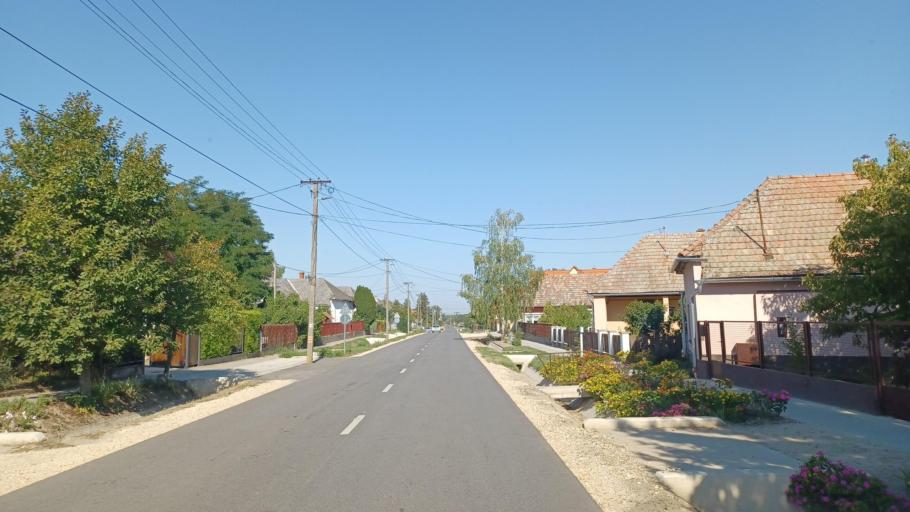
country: HU
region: Tolna
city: Nemetker
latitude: 46.7268
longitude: 18.7526
